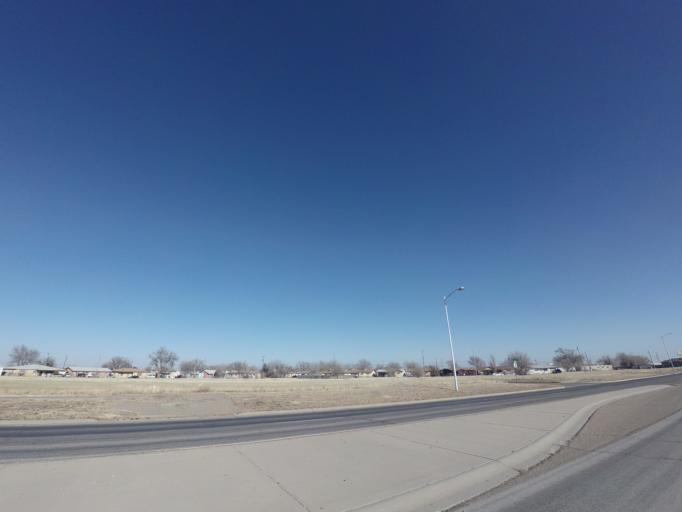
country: US
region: New Mexico
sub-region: Curry County
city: Clovis
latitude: 34.4023
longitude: -103.2435
